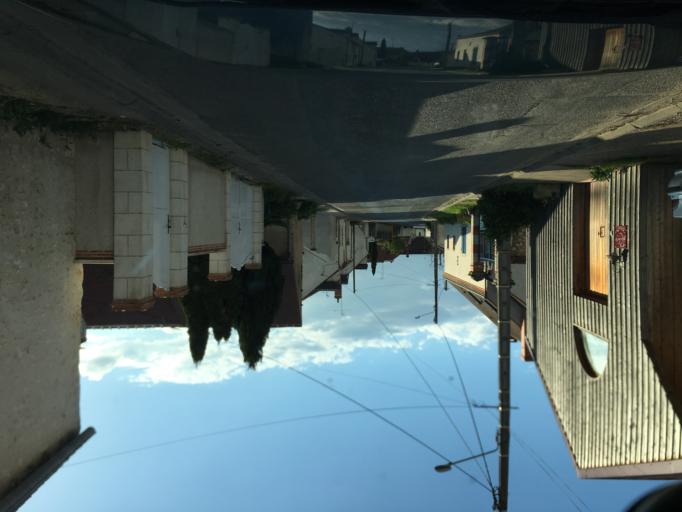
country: FR
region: Centre
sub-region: Departement du Loiret
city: Clery-Saint-Andre
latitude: 47.8346
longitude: 1.7664
